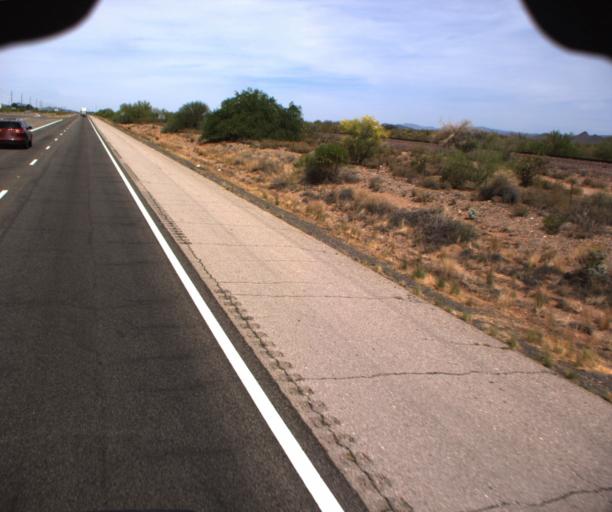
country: US
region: Arizona
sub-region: Maricopa County
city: Wickenburg
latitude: 33.8159
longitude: -112.5772
